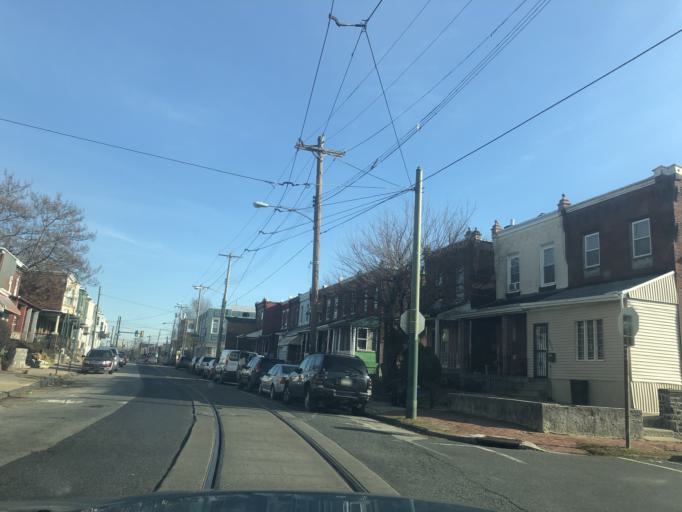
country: US
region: Pennsylvania
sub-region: Delaware County
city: Millbourne
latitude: 39.9699
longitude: -75.2413
